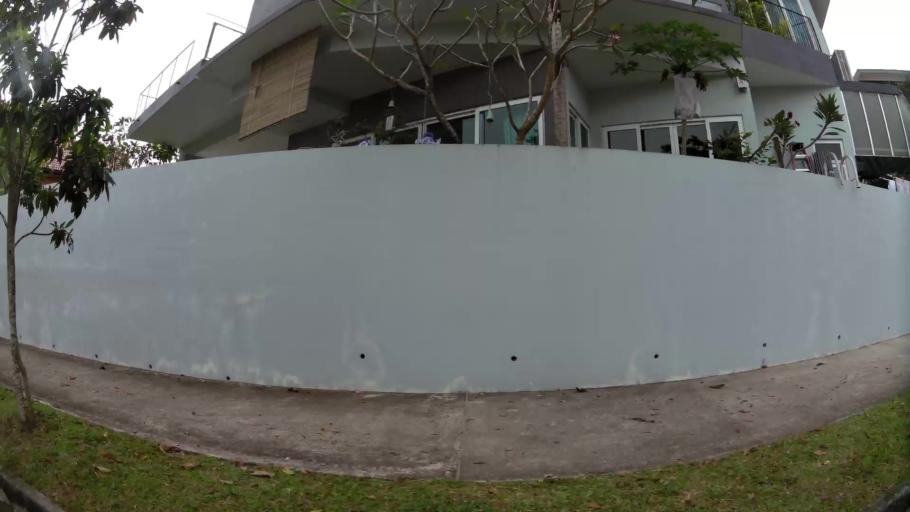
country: SG
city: Singapore
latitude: 1.3366
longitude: 103.7862
